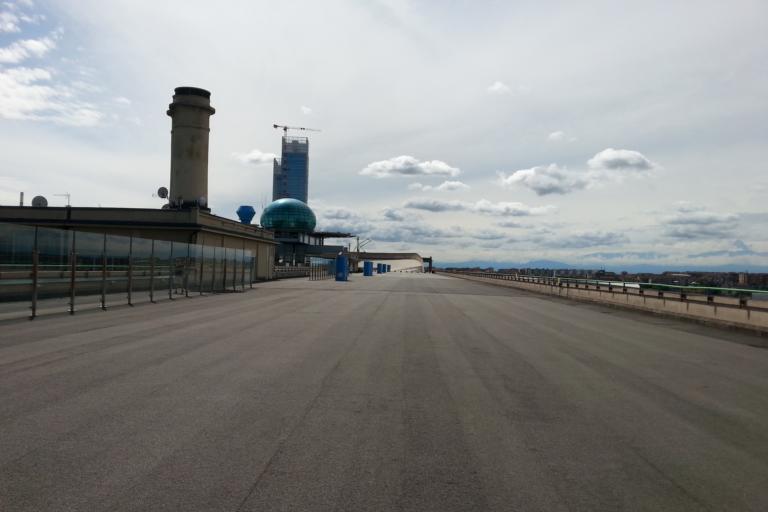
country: IT
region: Piedmont
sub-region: Provincia di Torino
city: Moncalieri
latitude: 45.0326
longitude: 7.6653
